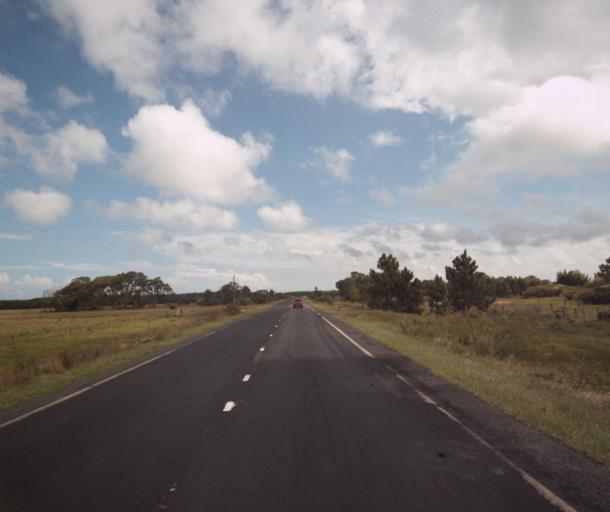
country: BR
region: Rio Grande do Sul
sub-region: Tapes
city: Tapes
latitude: -31.4073
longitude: -51.1671
